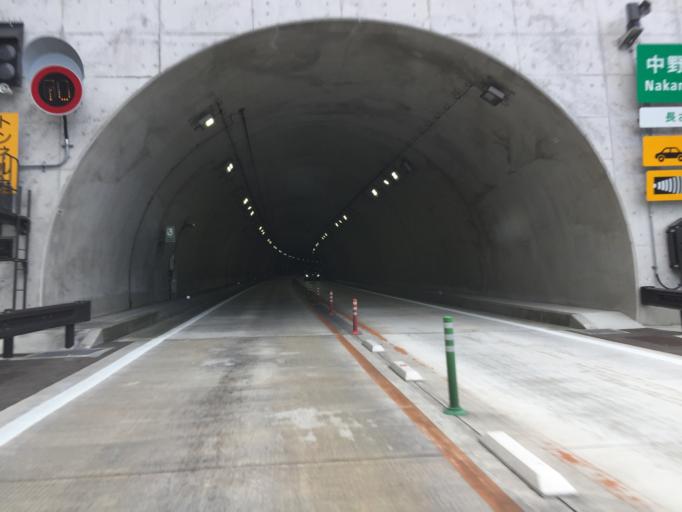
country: JP
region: Fukushima
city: Fukushima-shi
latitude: 37.8419
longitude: 140.3615
